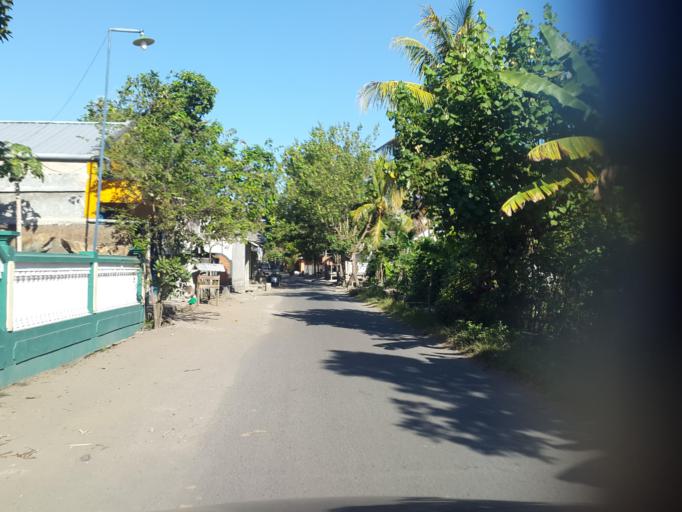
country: ID
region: West Nusa Tenggara
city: Jelateng Timur
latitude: -8.6834
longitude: 116.0898
